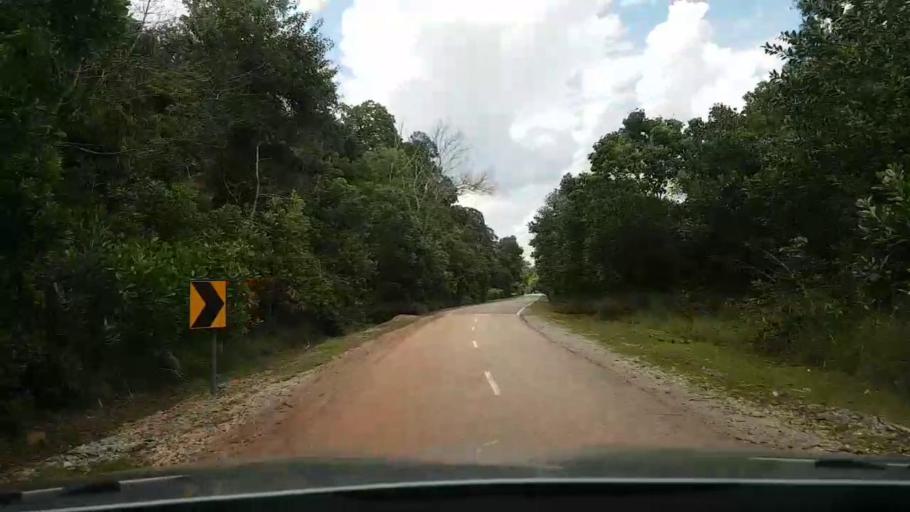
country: MY
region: Pahang
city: Pekan
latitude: 3.1455
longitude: 102.9700
